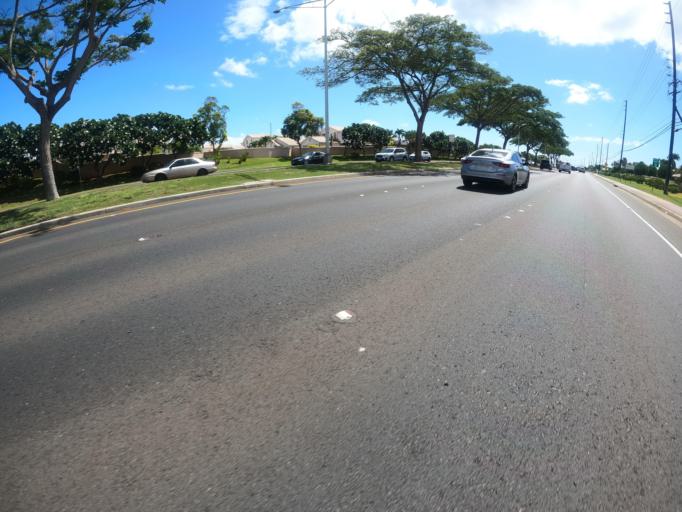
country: US
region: Hawaii
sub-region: Honolulu County
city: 'Ewa Gentry
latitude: 21.3376
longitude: -158.0242
